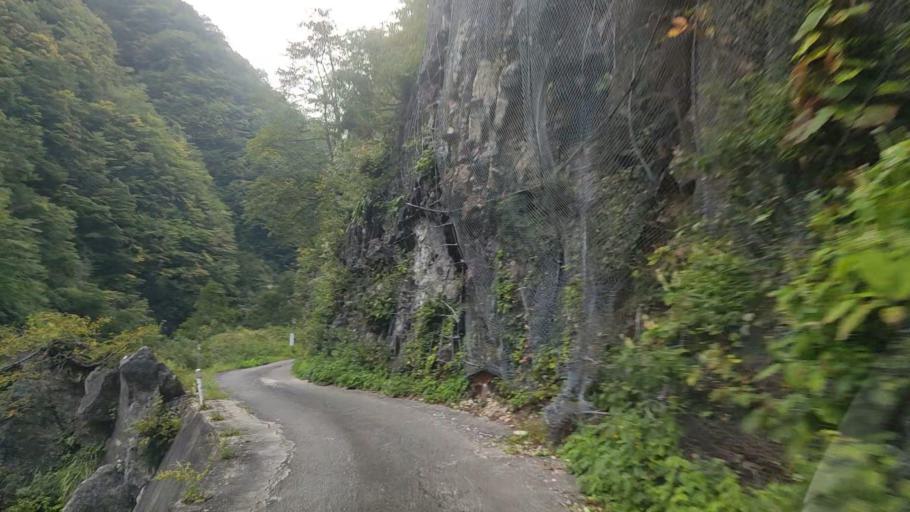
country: JP
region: Toyama
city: Yatsuomachi-higashikumisaka
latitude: 36.3919
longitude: 137.0798
